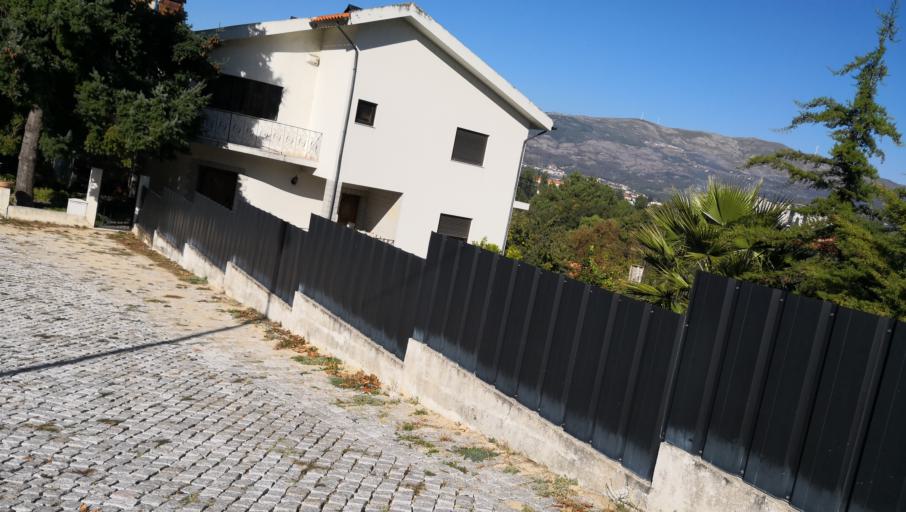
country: PT
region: Vila Real
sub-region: Vila Real
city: Vila Real
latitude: 41.3049
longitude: -7.7269
